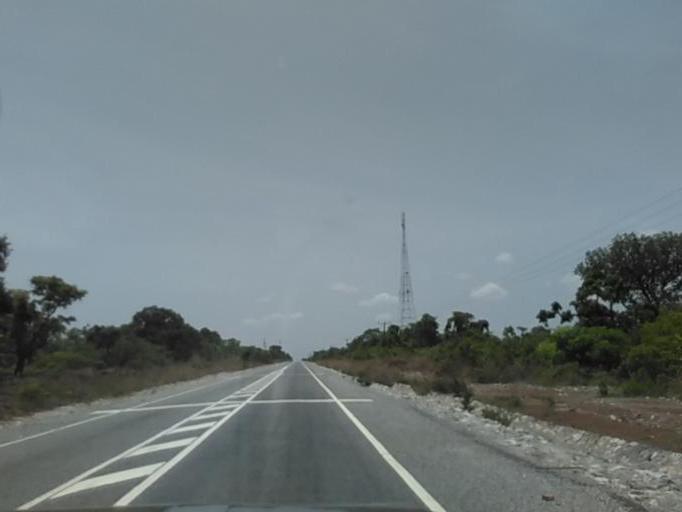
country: GH
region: Northern
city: Tamale
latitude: 9.1336
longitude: -1.5824
